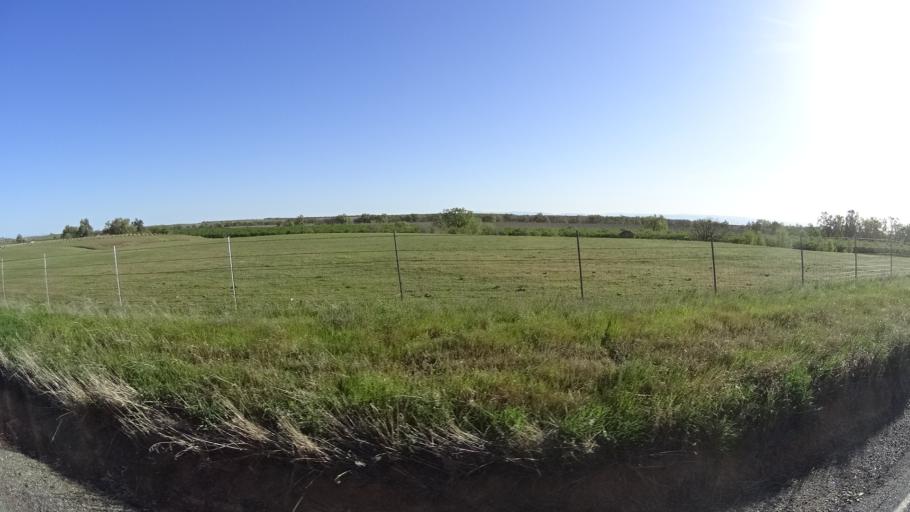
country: US
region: California
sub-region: Glenn County
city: Orland
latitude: 39.8001
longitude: -122.3227
